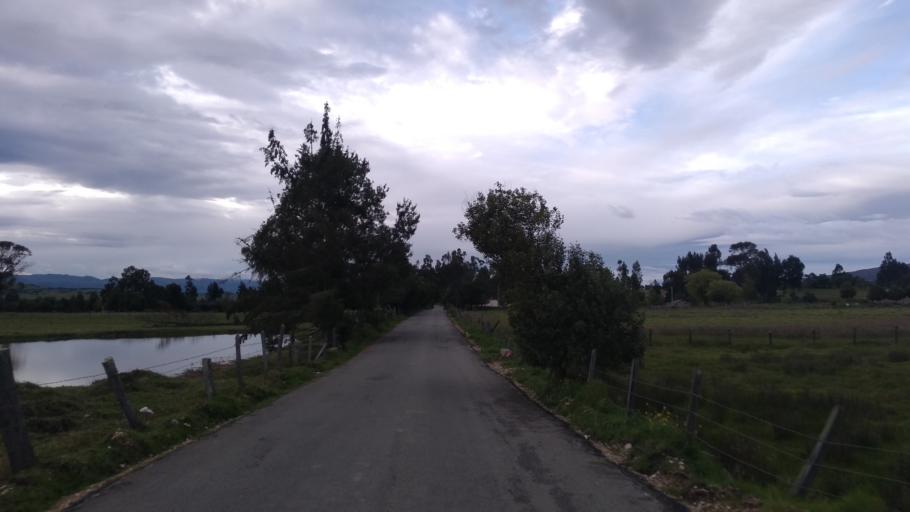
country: CO
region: Boyaca
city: Toca
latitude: 5.5837
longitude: -73.1832
